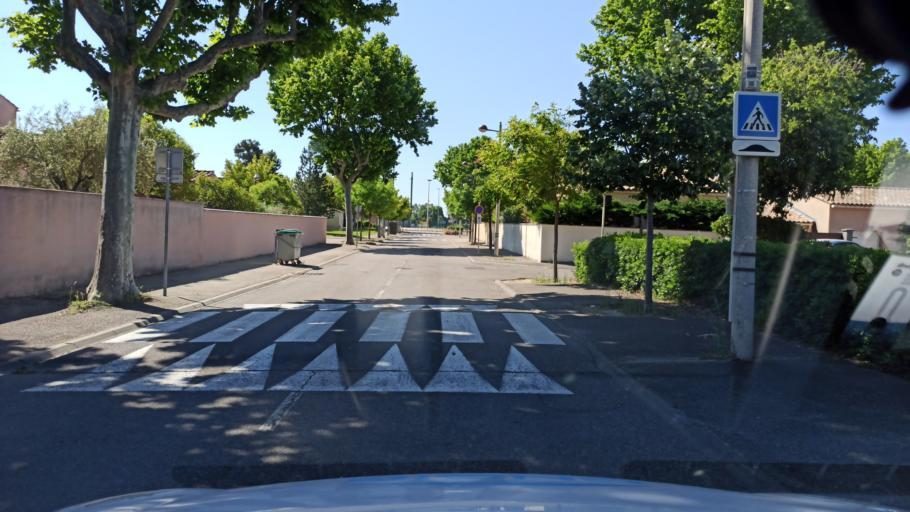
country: FR
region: Provence-Alpes-Cote d'Azur
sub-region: Departement du Vaucluse
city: Monteux
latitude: 44.0316
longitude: 5.0023
